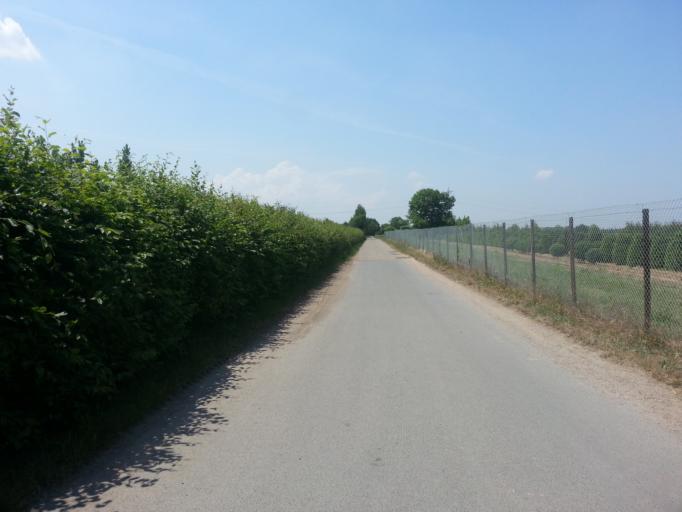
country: DE
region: Baden-Wuerttemberg
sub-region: Karlsruhe Region
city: Schriesheim
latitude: 49.4760
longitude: 8.6374
